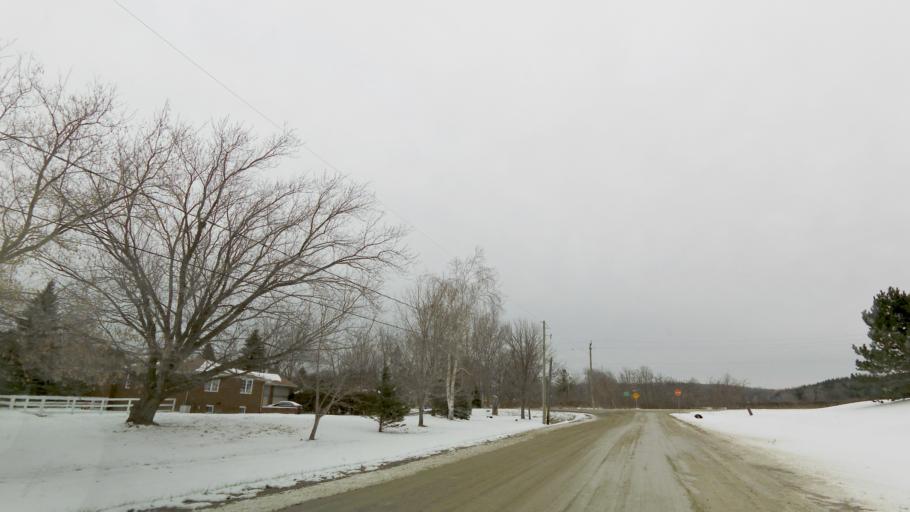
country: CA
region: Ontario
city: Bradford West Gwillimbury
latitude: 43.9847
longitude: -79.6223
